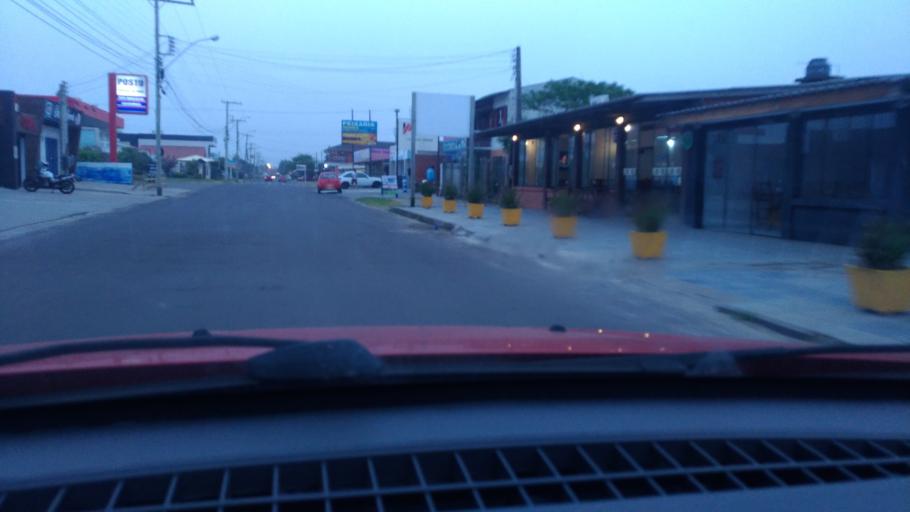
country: BR
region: Rio Grande do Sul
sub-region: Capao Da Canoa
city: Capao da Canoa
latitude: -29.8521
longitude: -50.0653
